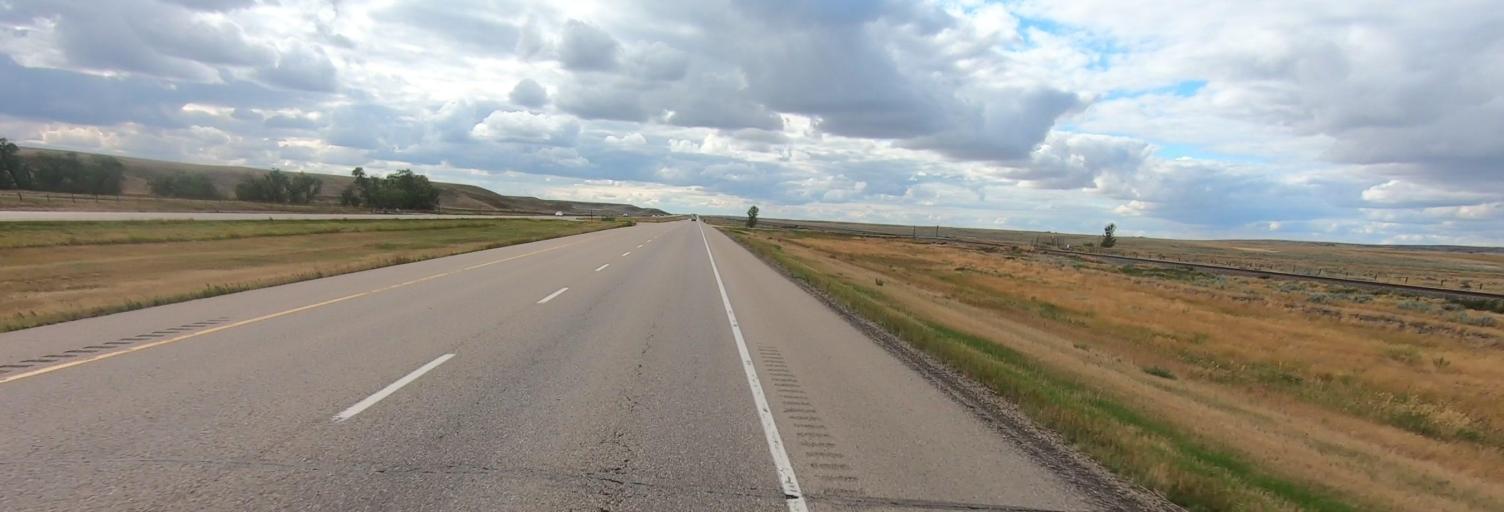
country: CA
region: Alberta
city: Medicine Hat
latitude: 49.9428
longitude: -110.1898
